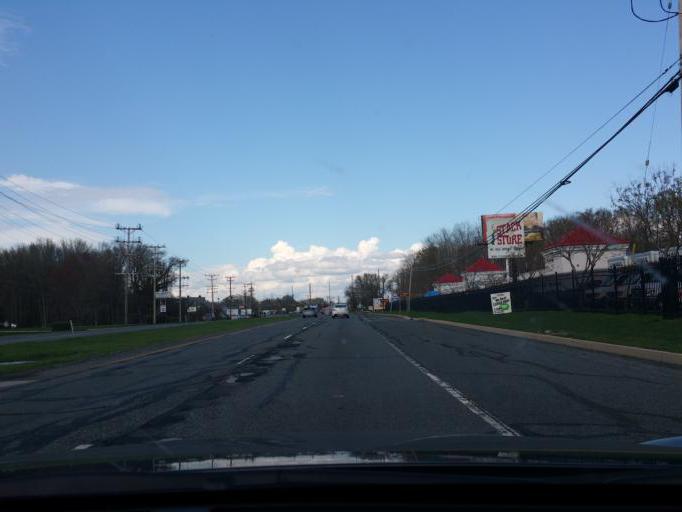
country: US
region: Maryland
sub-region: Harford County
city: Havre de Grace
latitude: 39.5331
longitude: -76.1202
